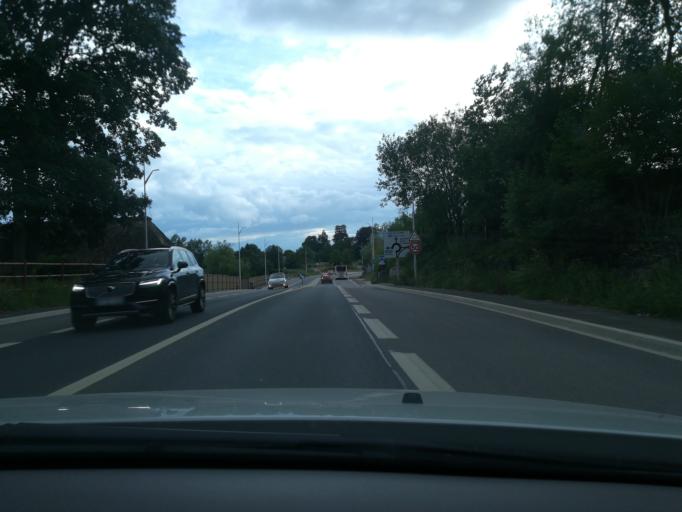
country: FR
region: Haute-Normandie
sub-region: Departement de la Seine-Maritime
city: Isneauville
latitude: 49.4843
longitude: 1.1352
